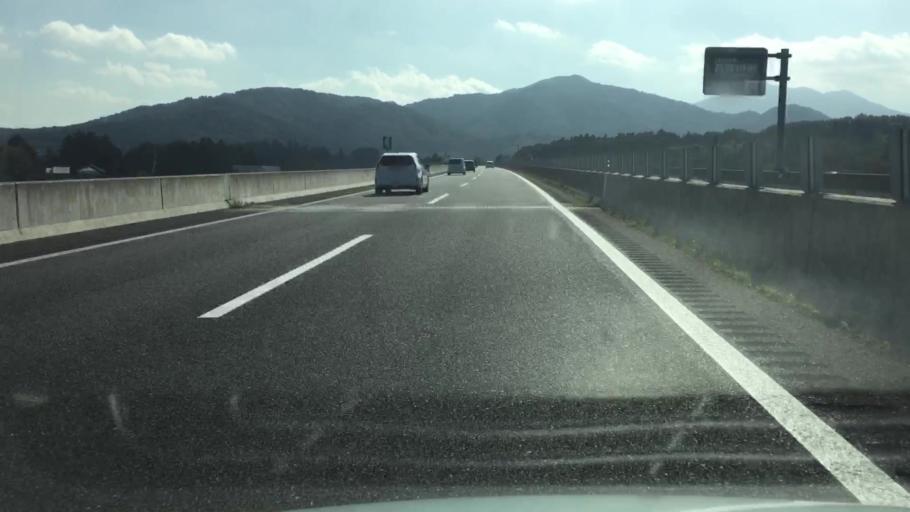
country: JP
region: Ibaraki
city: Iwase
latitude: 36.3567
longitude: 140.0894
